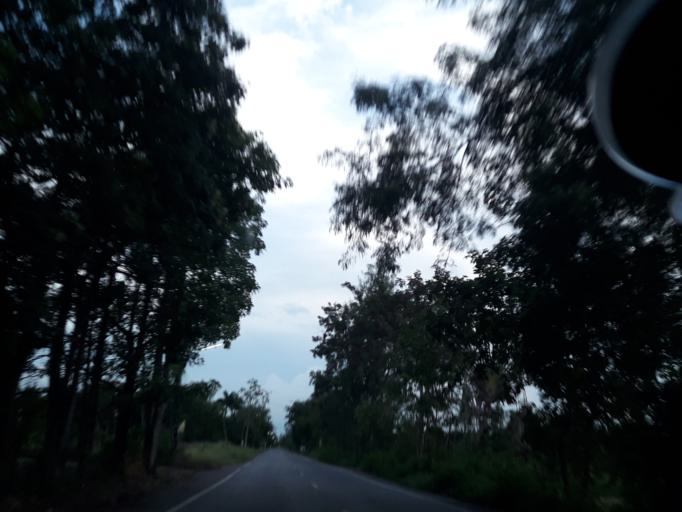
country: TH
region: Pathum Thani
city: Nong Suea
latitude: 14.1677
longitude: 100.8689
